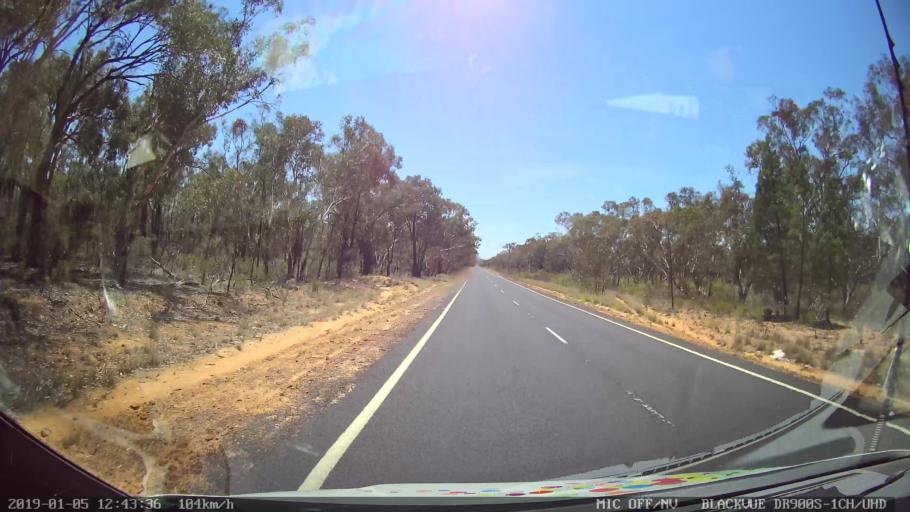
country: AU
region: New South Wales
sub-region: Warrumbungle Shire
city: Coonabarabran
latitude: -31.1463
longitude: 149.5263
